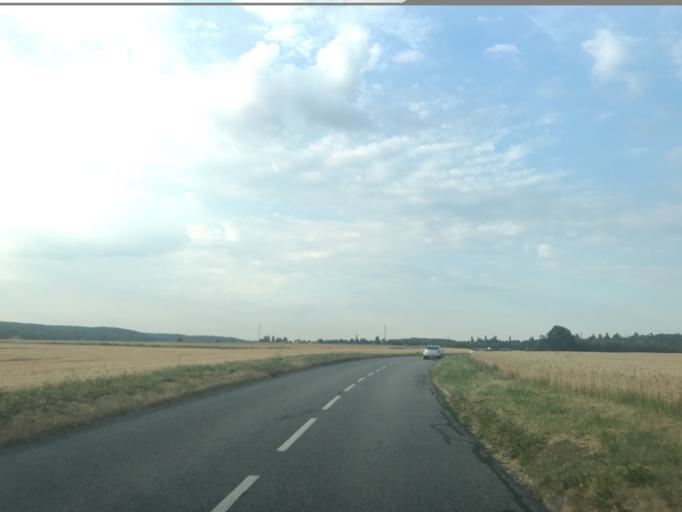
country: FR
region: Ile-de-France
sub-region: Departement des Yvelines
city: Jouars-Pontchartrain
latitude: 48.7914
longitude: 1.8711
